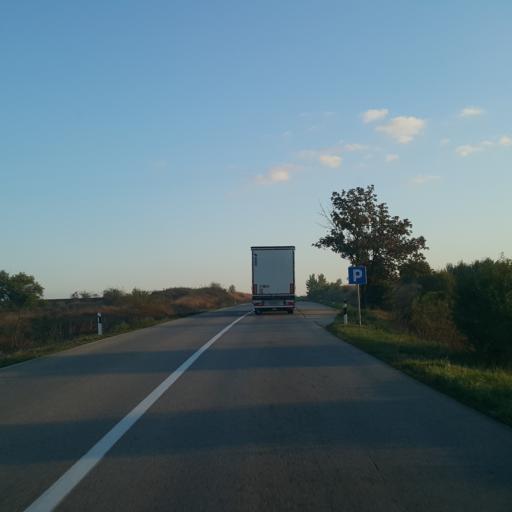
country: RS
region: Central Serbia
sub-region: Zajecarski Okrug
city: Zajecar
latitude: 44.0617
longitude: 22.3334
